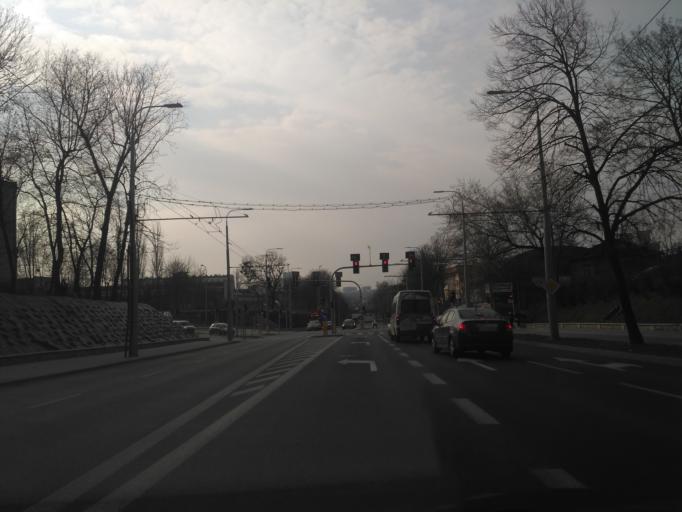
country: PL
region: Lublin Voivodeship
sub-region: Powiat lubelski
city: Lublin
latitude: 51.2344
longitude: 22.5827
